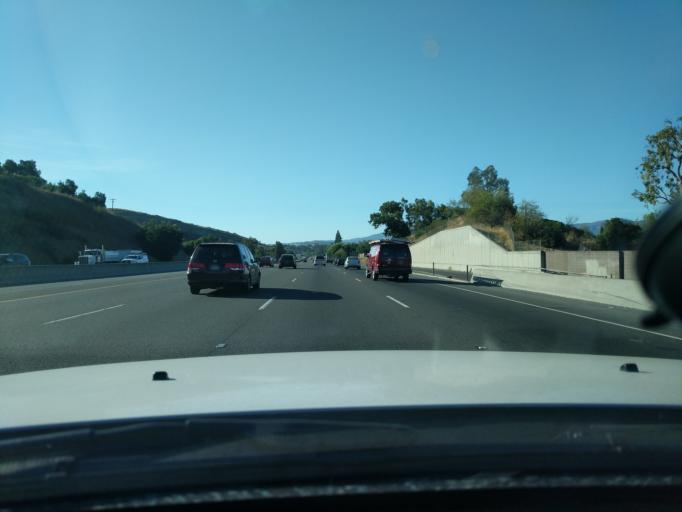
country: US
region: California
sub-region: Santa Clara County
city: Seven Trees
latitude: 37.2925
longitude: -121.8100
